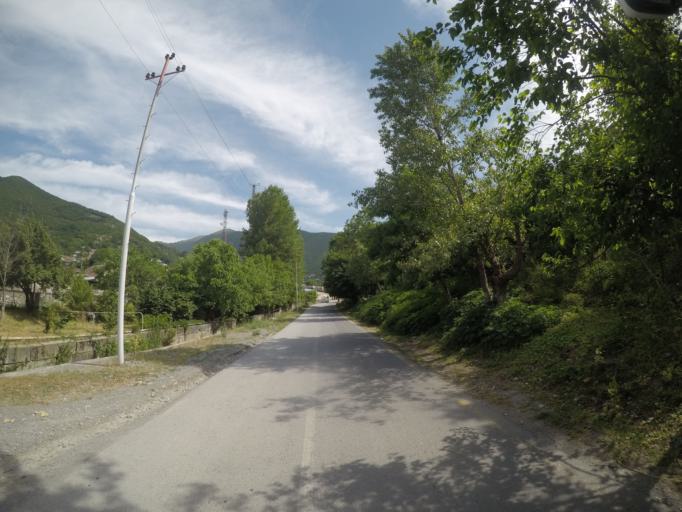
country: AZ
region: Shaki City
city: Sheki
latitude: 41.2470
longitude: 47.1888
